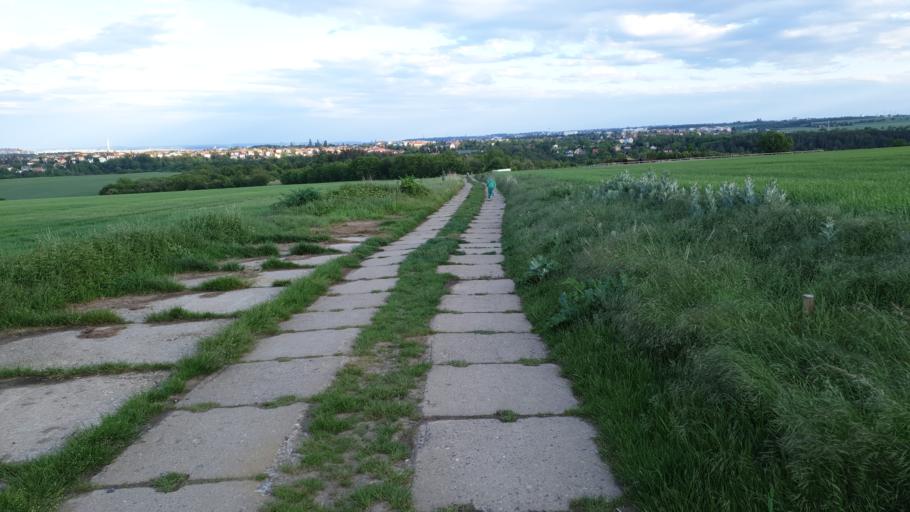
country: CZ
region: Central Bohemia
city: Roztoky
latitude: 50.1539
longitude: 14.3741
